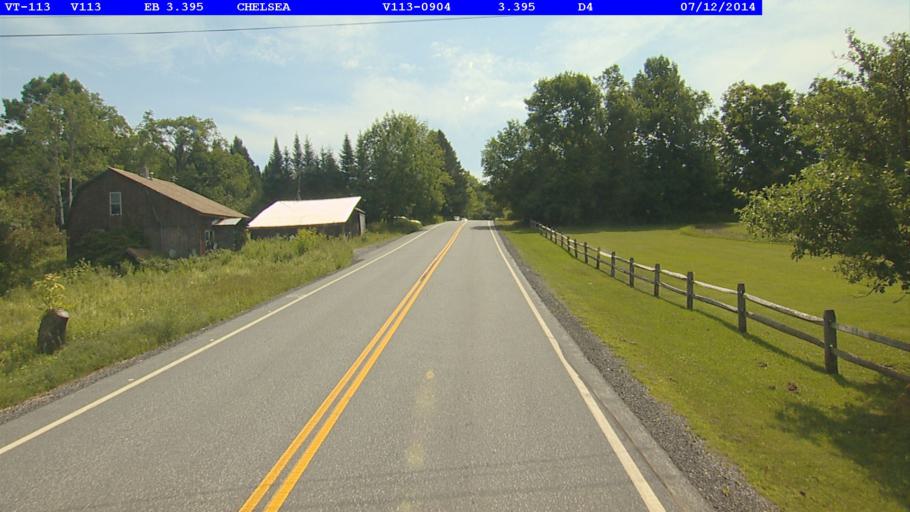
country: US
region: Vermont
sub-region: Orange County
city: Chelsea
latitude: 43.9921
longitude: -72.3852
